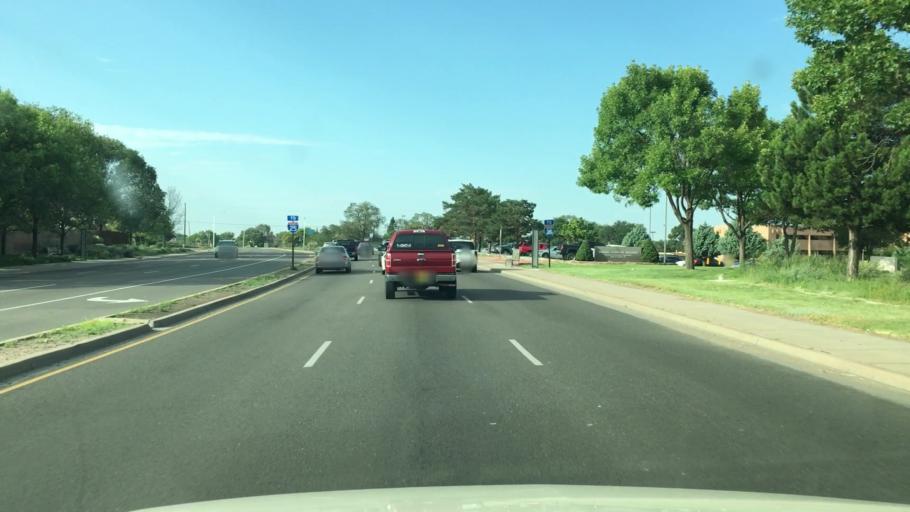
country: US
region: New Mexico
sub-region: Santa Fe County
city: Santa Fe
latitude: 35.6706
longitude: -105.9555
